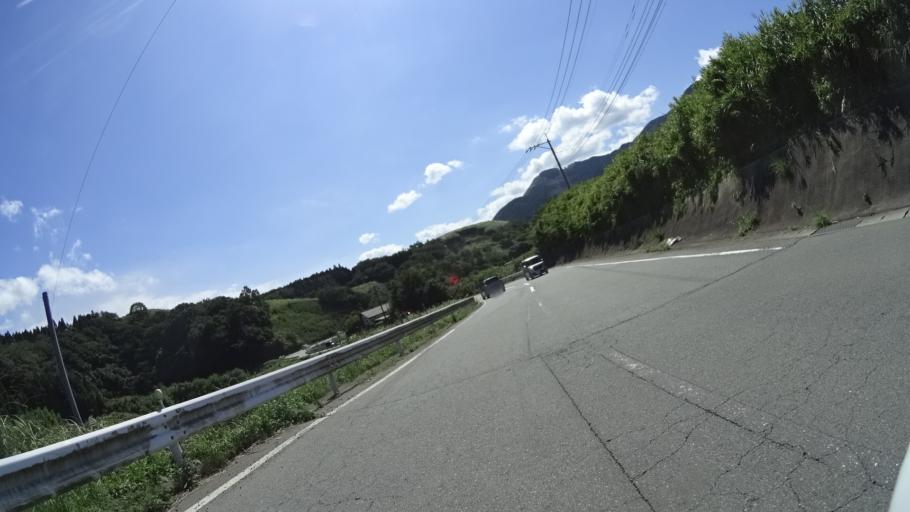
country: JP
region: Kumamoto
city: Aso
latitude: 32.8996
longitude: 130.9950
